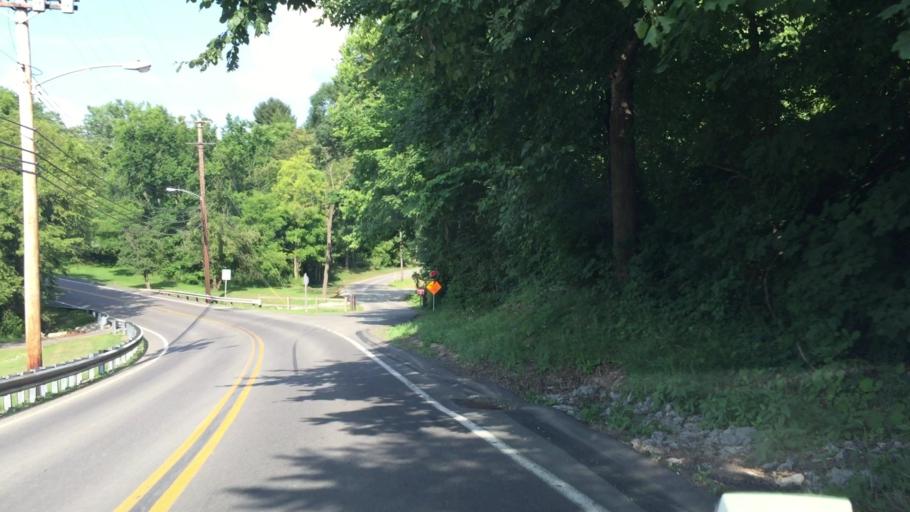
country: US
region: Pennsylvania
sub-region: Allegheny County
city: Coraopolis
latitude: 40.4880
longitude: -80.1886
